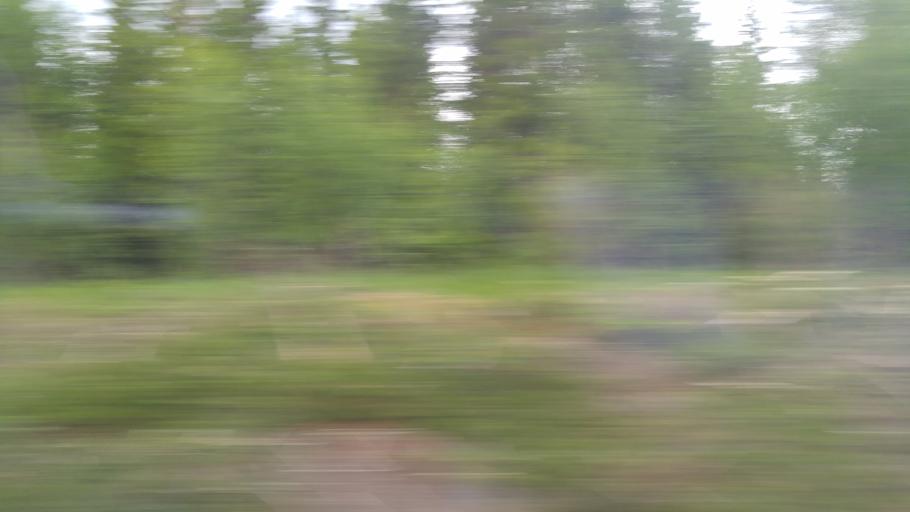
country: SE
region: Jaemtland
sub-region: Are Kommun
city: Are
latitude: 63.3034
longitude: 12.4245
